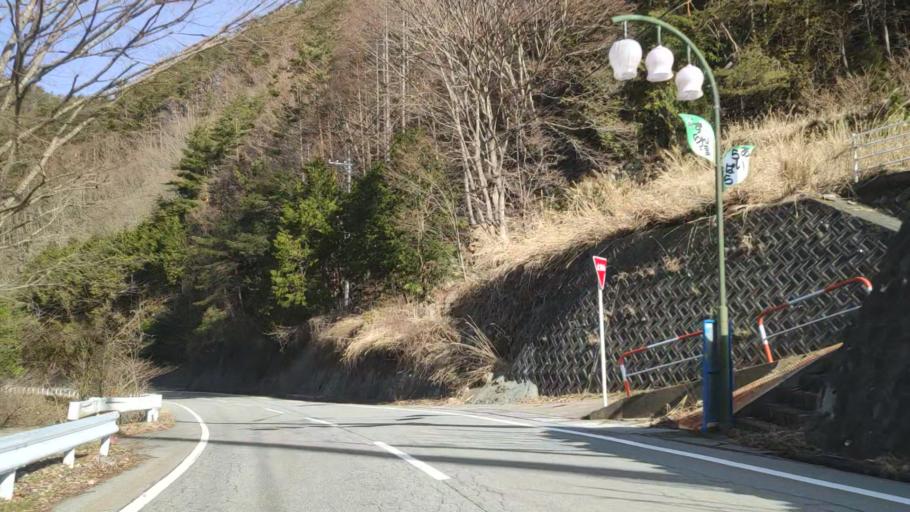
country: JP
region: Yamanashi
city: Fujikawaguchiko
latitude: 35.5547
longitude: 138.6733
